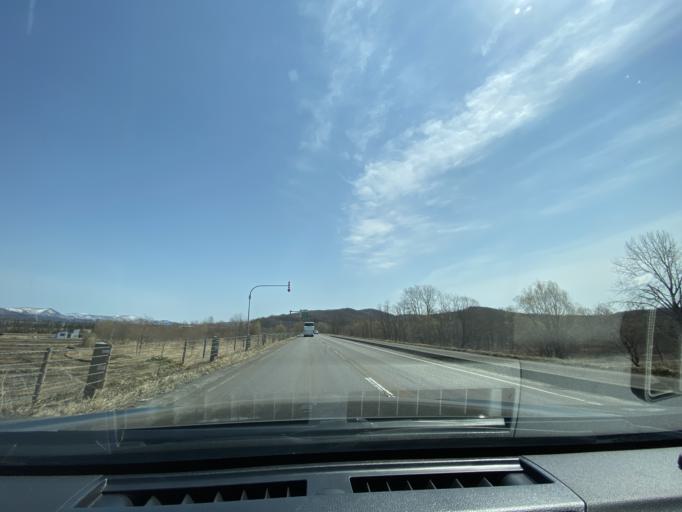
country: JP
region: Hokkaido
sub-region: Asahikawa-shi
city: Asahikawa
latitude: 43.8987
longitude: 142.5469
